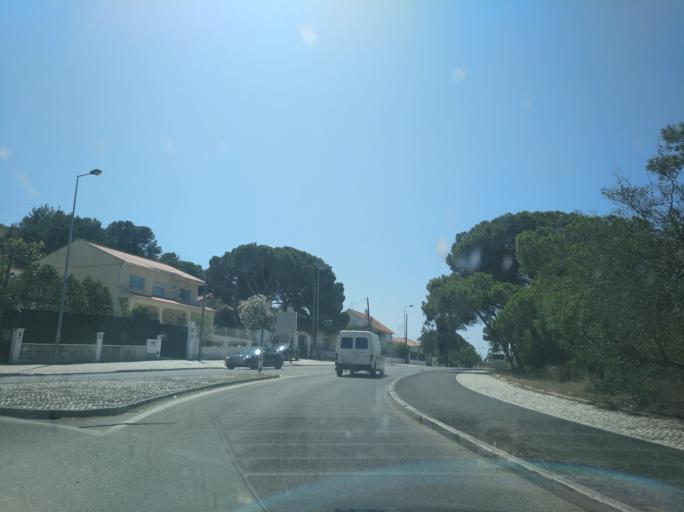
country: PT
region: Setubal
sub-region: Almada
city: Trafaria
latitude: 38.6676
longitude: -9.2404
